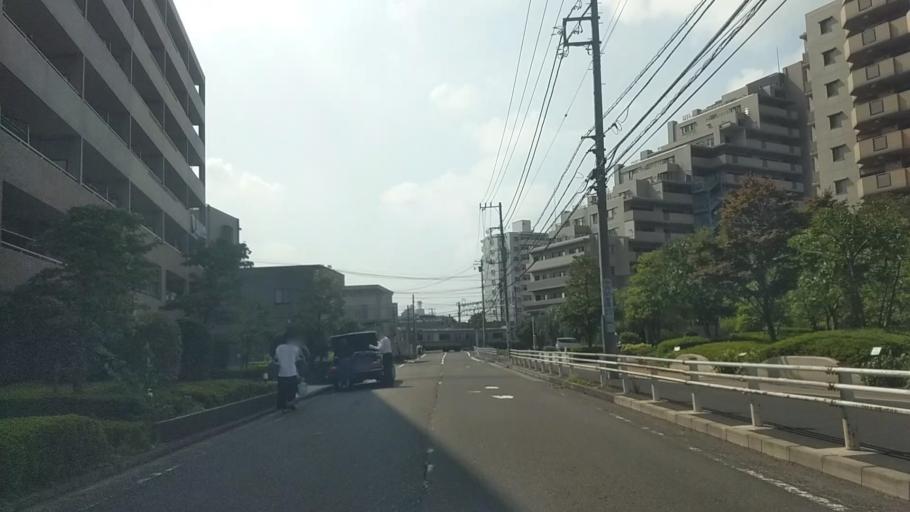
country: JP
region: Kanagawa
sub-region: Kawasaki-shi
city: Kawasaki
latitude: 35.5247
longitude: 139.6872
